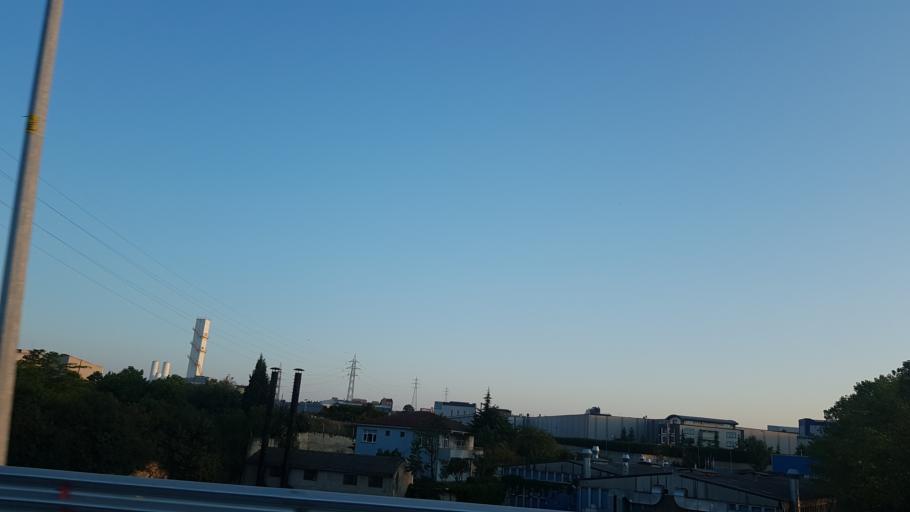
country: TR
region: Kocaeli
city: Tavsanli
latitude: 40.7993
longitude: 29.5154
